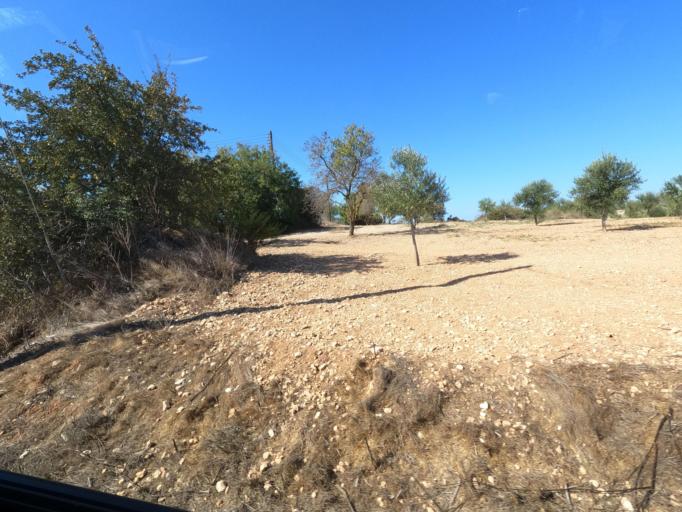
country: CY
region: Pafos
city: Mesogi
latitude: 34.8055
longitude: 32.4902
